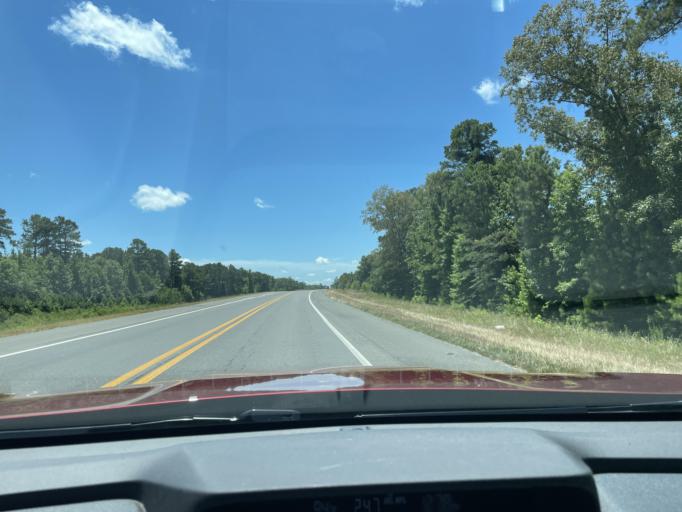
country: US
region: Arkansas
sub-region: Jefferson County
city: Pine Bluff
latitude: 34.1319
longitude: -91.9717
